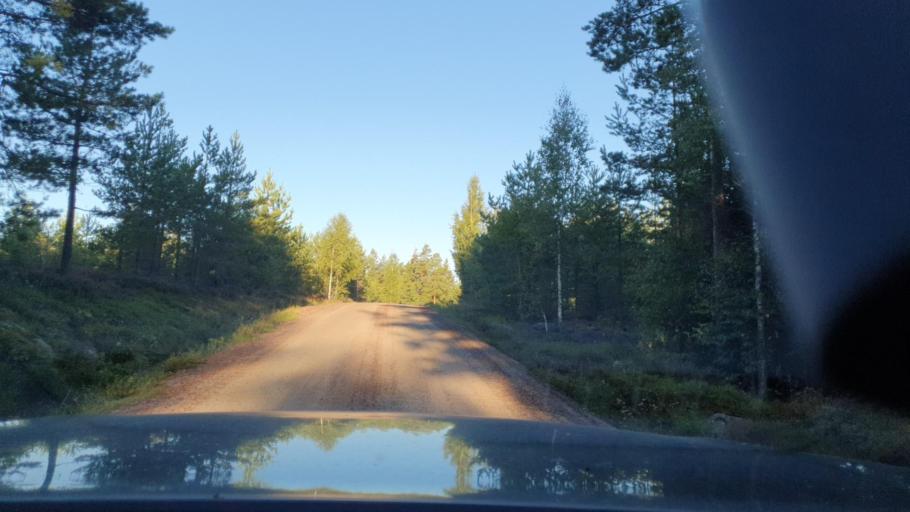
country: SE
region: Vaermland
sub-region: Karlstads Kommun
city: Skattkarr
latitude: 59.4758
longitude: 13.7133
